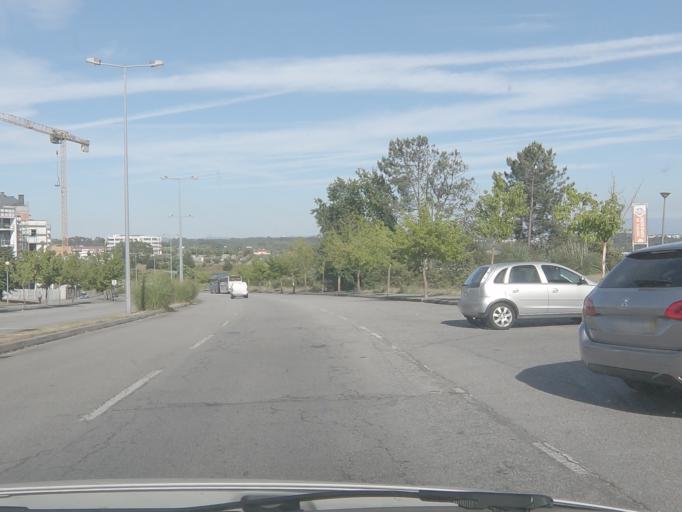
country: PT
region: Viseu
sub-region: Viseu
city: Viseu
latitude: 40.6411
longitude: -7.9172
